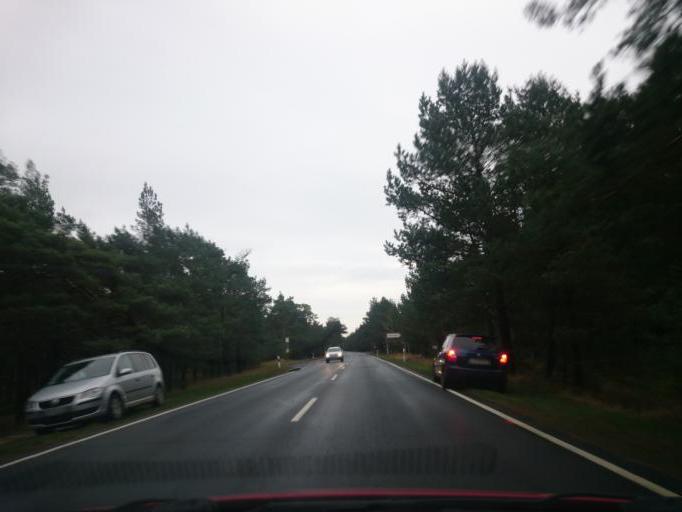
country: DE
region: Mecklenburg-Vorpommern
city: Altenkirchen
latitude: 54.5899
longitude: 13.3966
